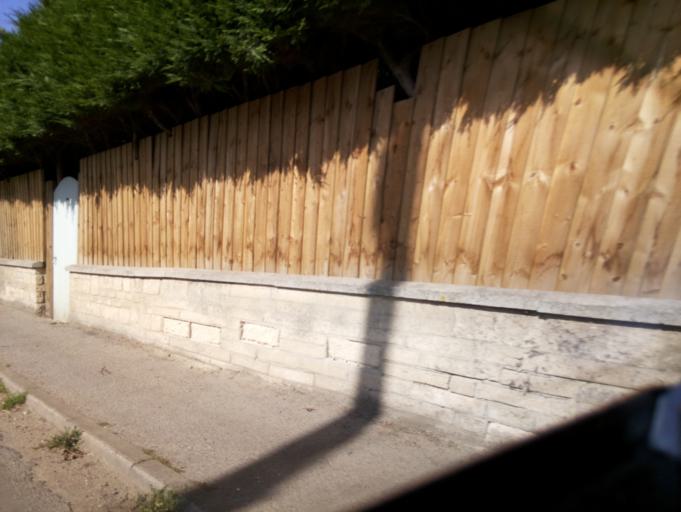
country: GB
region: England
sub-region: Oxfordshire
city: Bampton
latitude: 51.7284
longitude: -1.5076
